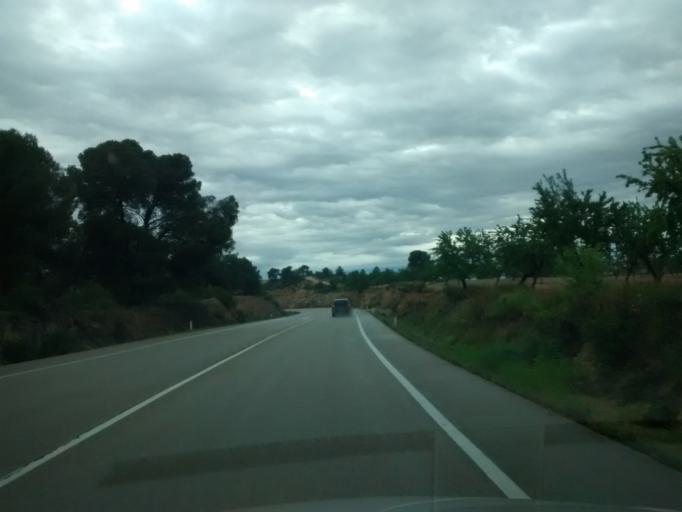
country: ES
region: Aragon
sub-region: Provincia de Zaragoza
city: Maella
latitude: 41.1548
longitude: 0.0963
